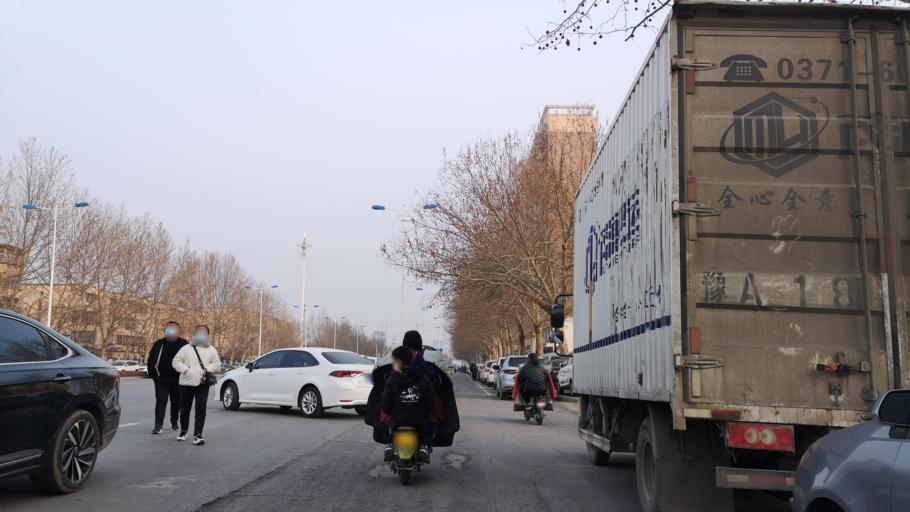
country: CN
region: Henan Sheng
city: Zhongyuanlu
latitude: 35.7651
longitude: 115.0942
